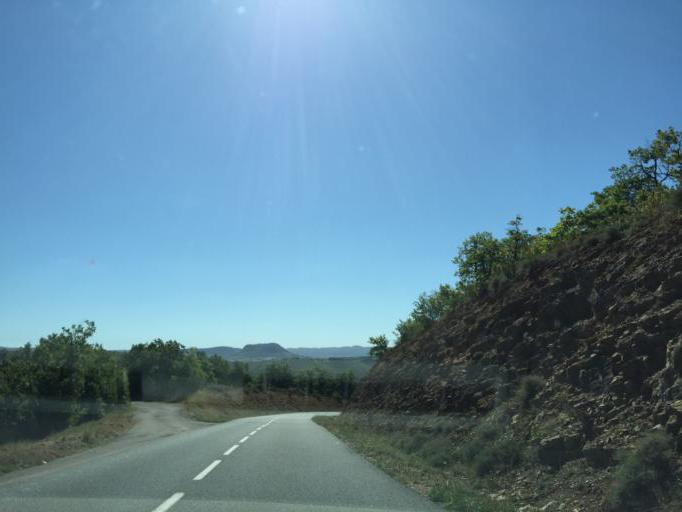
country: FR
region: Midi-Pyrenees
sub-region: Departement de l'Aveyron
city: Saint-Georges-de-Luzencon
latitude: 44.0713
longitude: 2.9041
